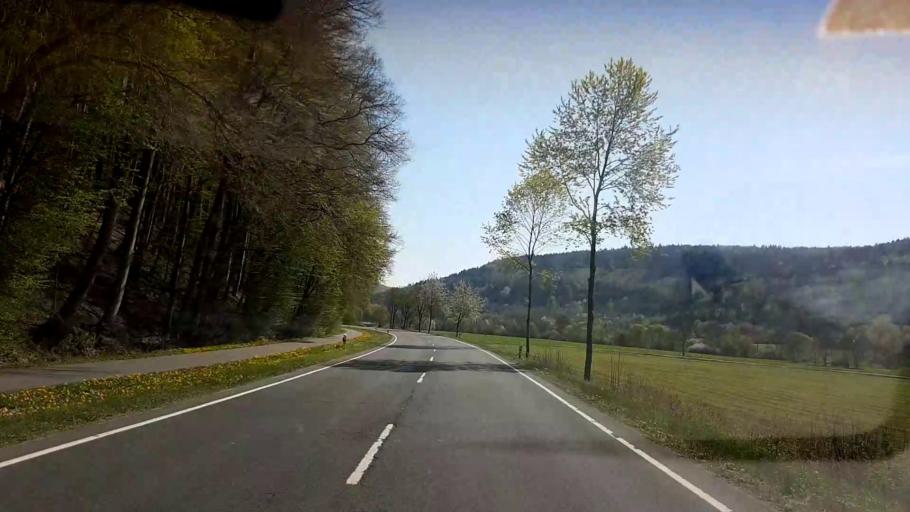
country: DE
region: Bavaria
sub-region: Upper Franconia
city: Unterleinleiter
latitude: 49.8105
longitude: 11.1950
